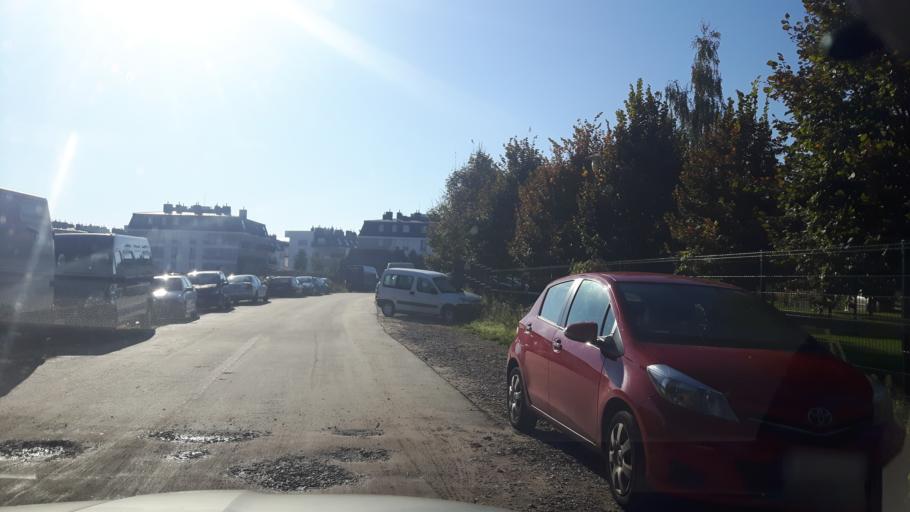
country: PL
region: Masovian Voivodeship
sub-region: Powiat legionowski
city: Stanislawow Pierwszy
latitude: 52.3626
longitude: 21.0383
